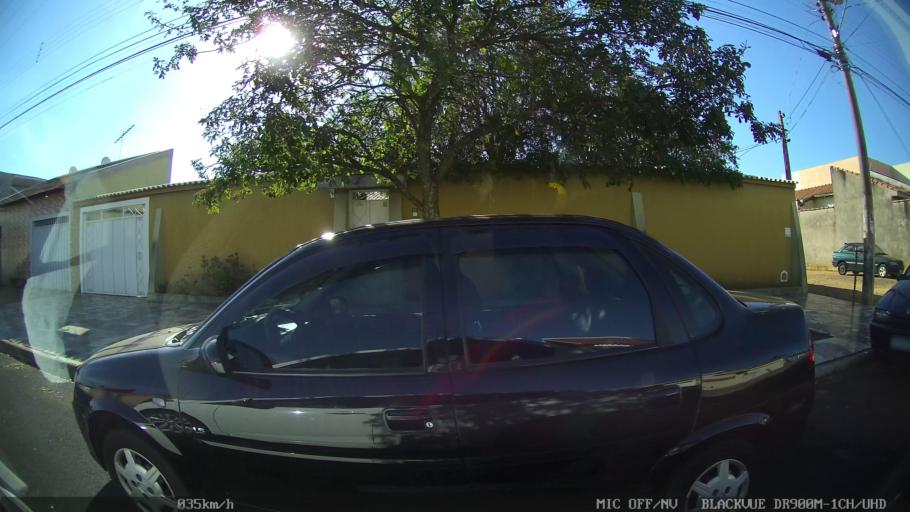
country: BR
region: Sao Paulo
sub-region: Franca
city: Franca
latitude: -20.5104
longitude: -47.4196
